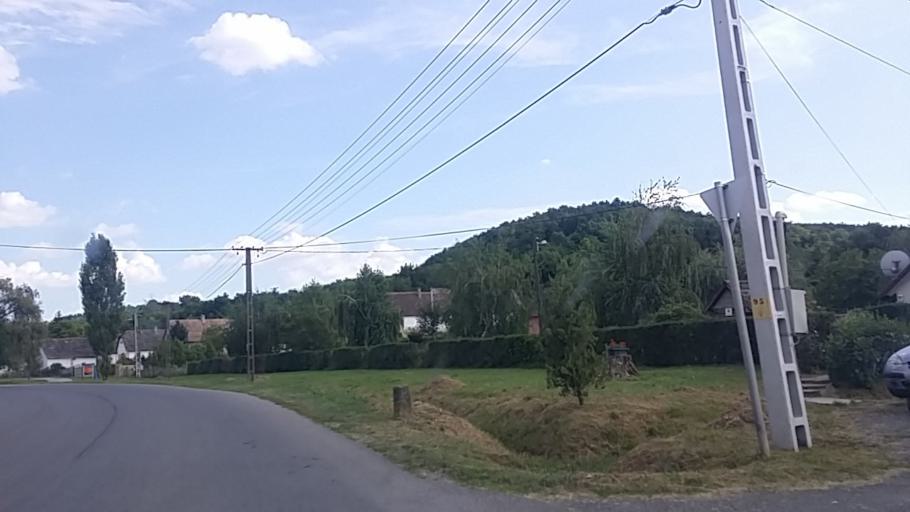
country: HU
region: Tolna
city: Gyonk
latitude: 46.5254
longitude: 18.5162
